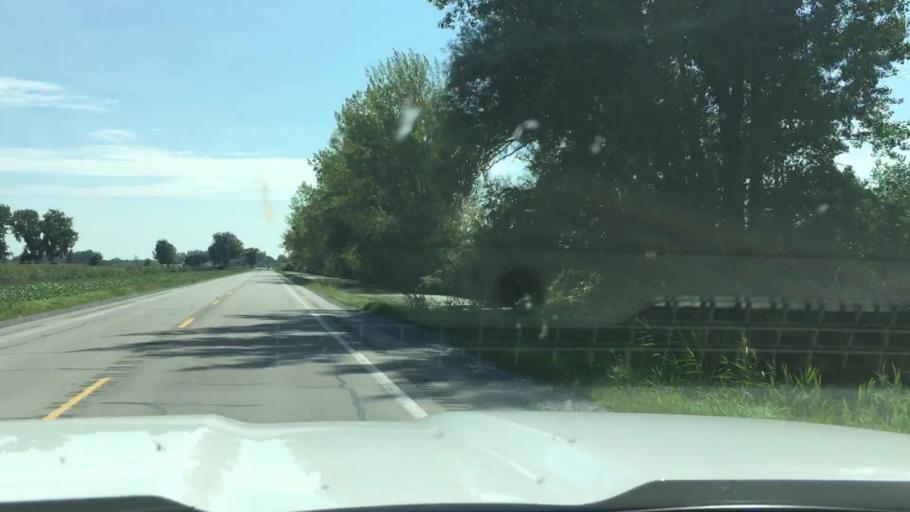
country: US
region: Michigan
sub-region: Tuscola County
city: Reese
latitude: 43.5828
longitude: -83.7095
